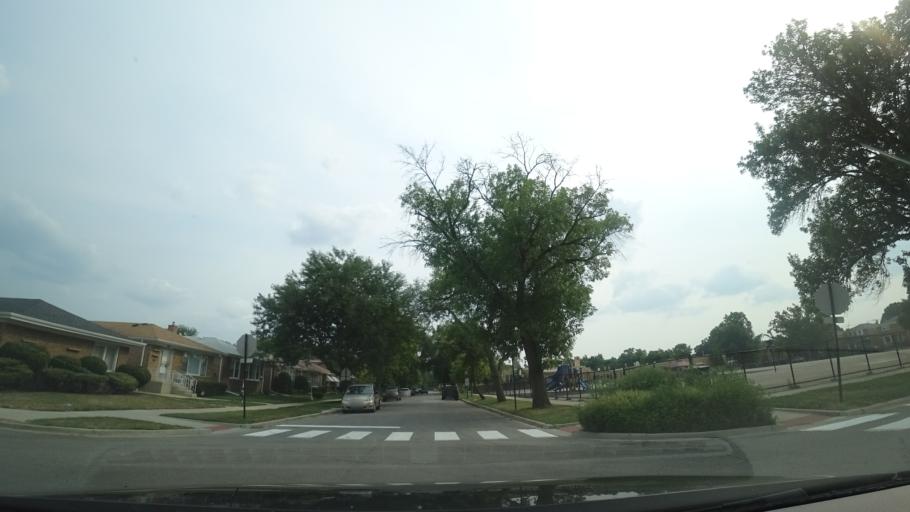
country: US
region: Illinois
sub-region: Cook County
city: Lincolnwood
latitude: 41.9956
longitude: -87.7238
